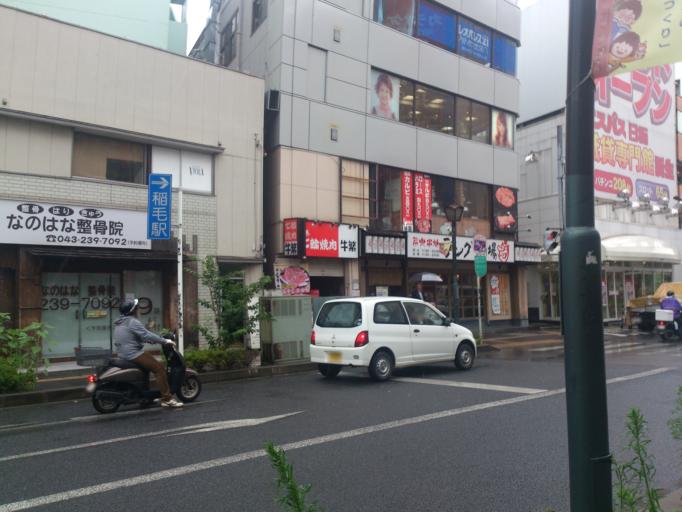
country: JP
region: Chiba
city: Chiba
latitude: 35.6382
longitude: 140.0925
